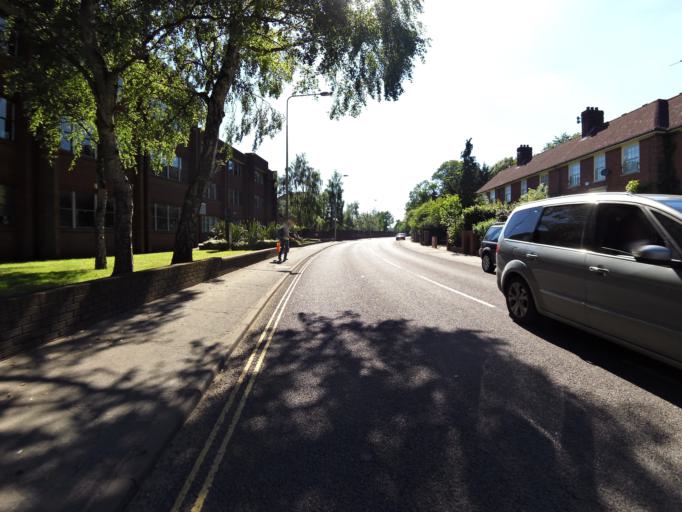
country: GB
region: England
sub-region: Norfolk
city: Thorpe Hamlet
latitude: 52.6250
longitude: 1.3194
